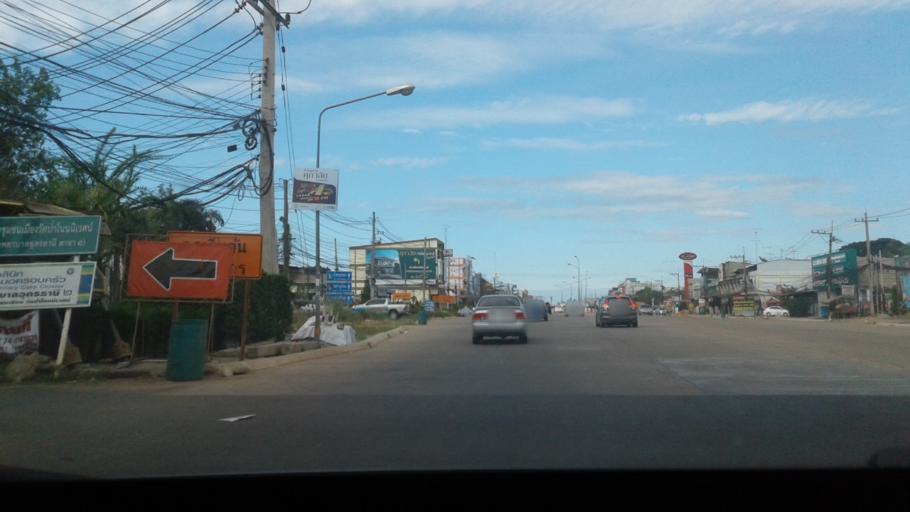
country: TH
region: Changwat Udon Thani
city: Udon Thani
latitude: 17.4284
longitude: 102.7910
